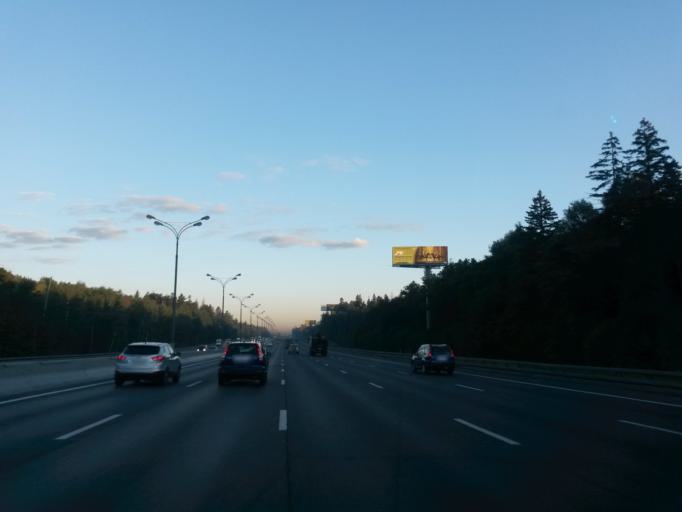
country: RU
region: Moscow
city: Gol'yanovo
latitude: 55.8478
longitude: 37.7936
